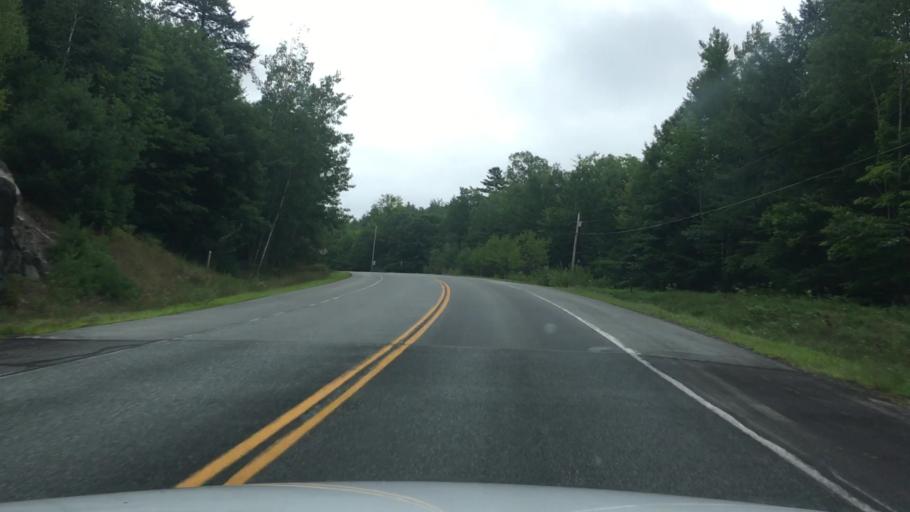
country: US
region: Maine
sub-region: Penobscot County
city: Bradley
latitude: 44.8192
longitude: -68.5024
